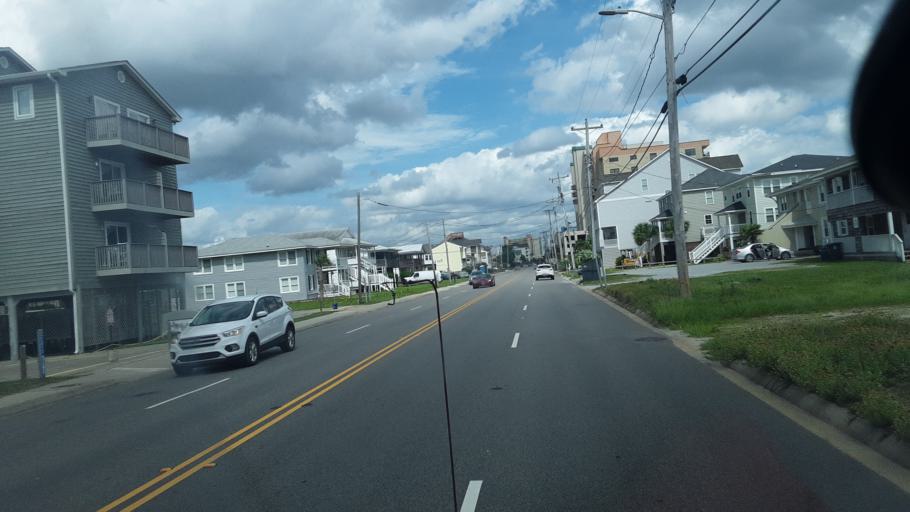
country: US
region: South Carolina
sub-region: Horry County
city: North Myrtle Beach
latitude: 33.8116
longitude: -78.6910
